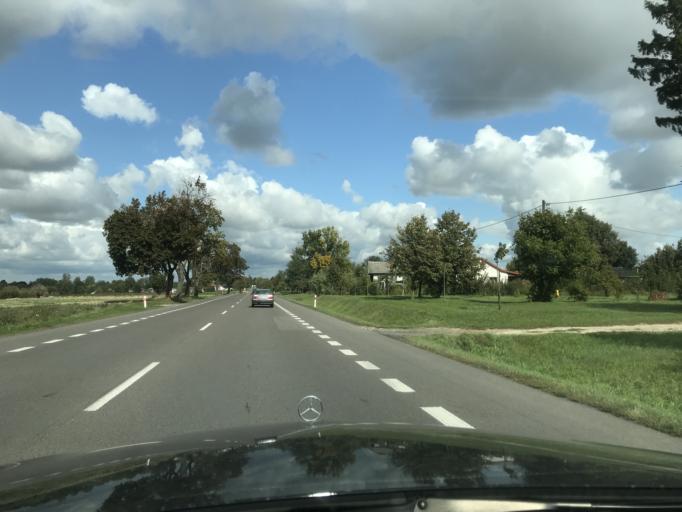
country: PL
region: Lublin Voivodeship
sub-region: Powiat krasnicki
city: Wilkolaz
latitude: 51.0496
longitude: 22.3813
